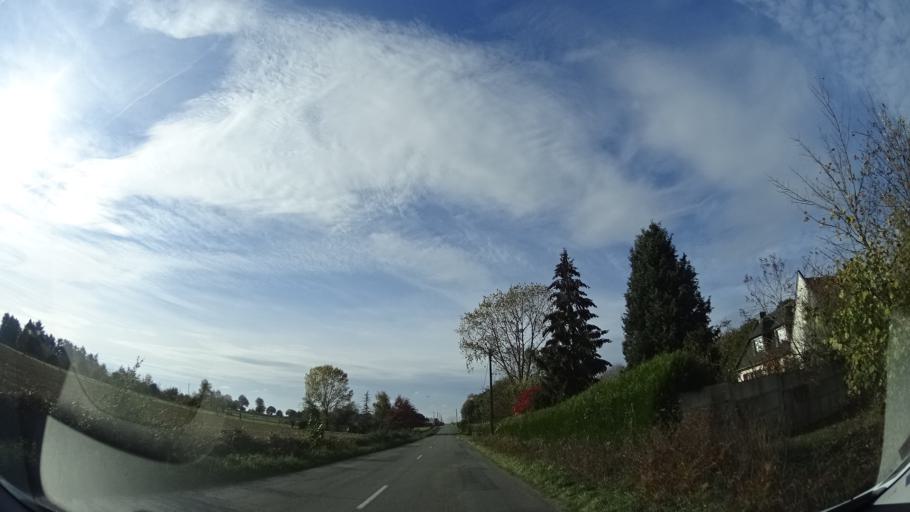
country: FR
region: Brittany
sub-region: Departement d'Ille-et-Vilaine
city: Romille
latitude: 48.2164
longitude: -1.8558
